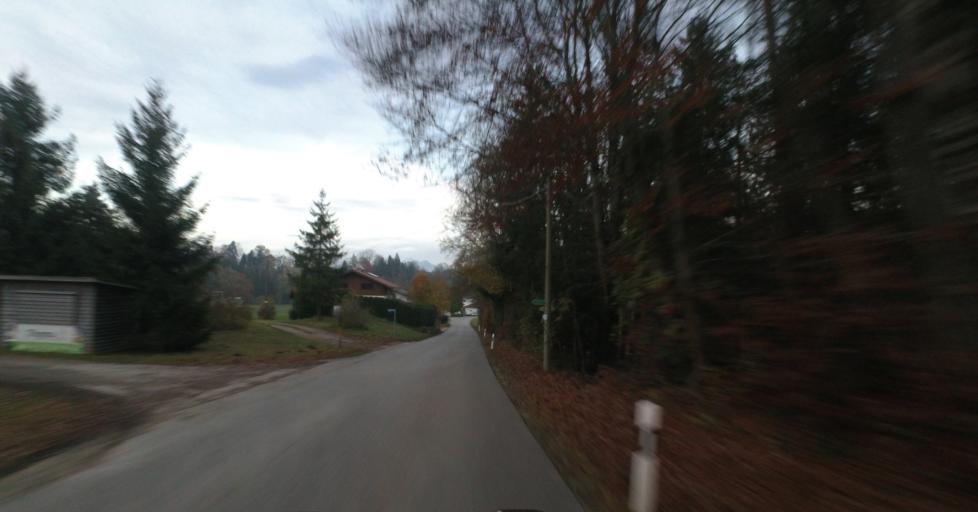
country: DE
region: Bavaria
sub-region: Upper Bavaria
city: Prien am Chiemsee
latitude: 47.8408
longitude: 12.3208
